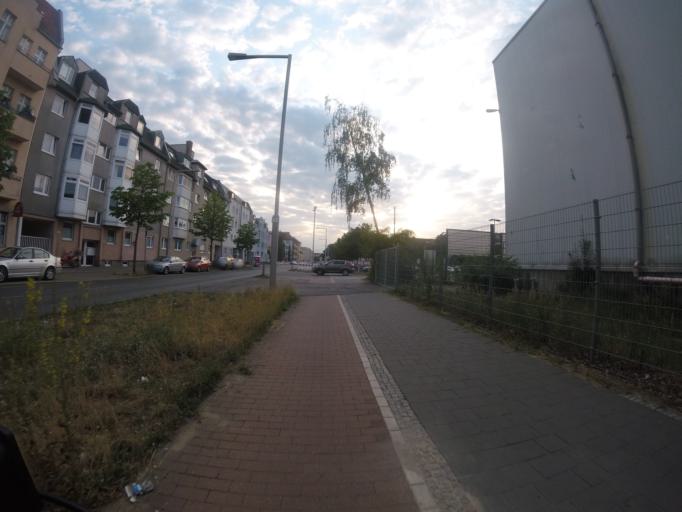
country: DE
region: Berlin
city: Hakenfelde
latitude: 52.5609
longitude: 13.2144
